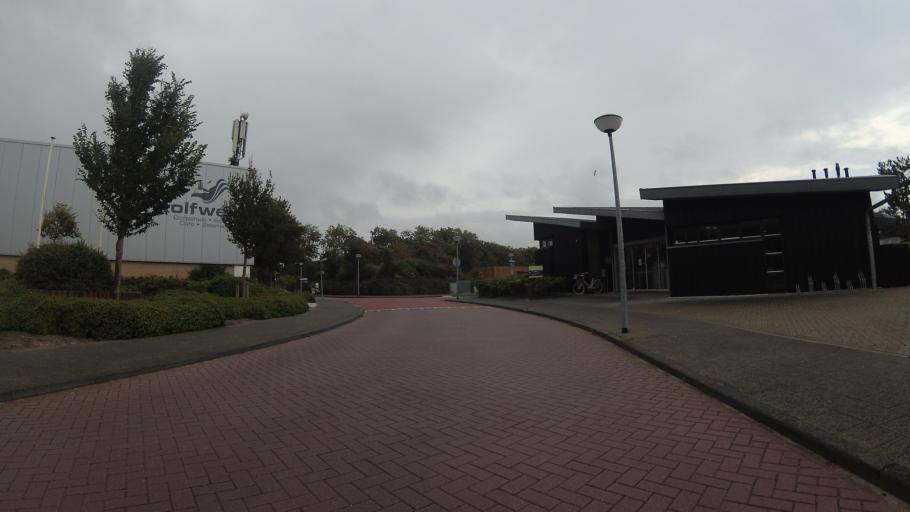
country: NL
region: North Holland
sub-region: Gemeente Schagen
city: Schagen
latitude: 52.8363
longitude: 4.6992
